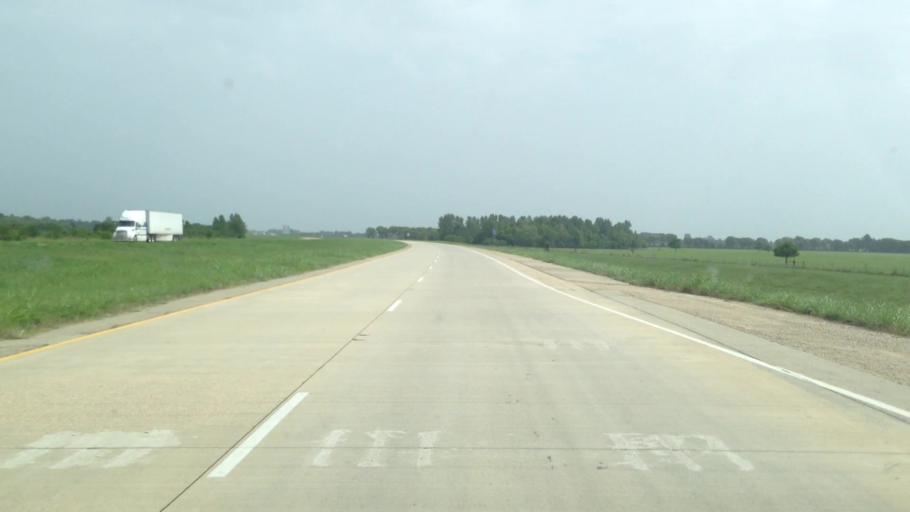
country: US
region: Louisiana
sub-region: Caddo Parish
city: Vivian
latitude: 32.8591
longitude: -93.8611
